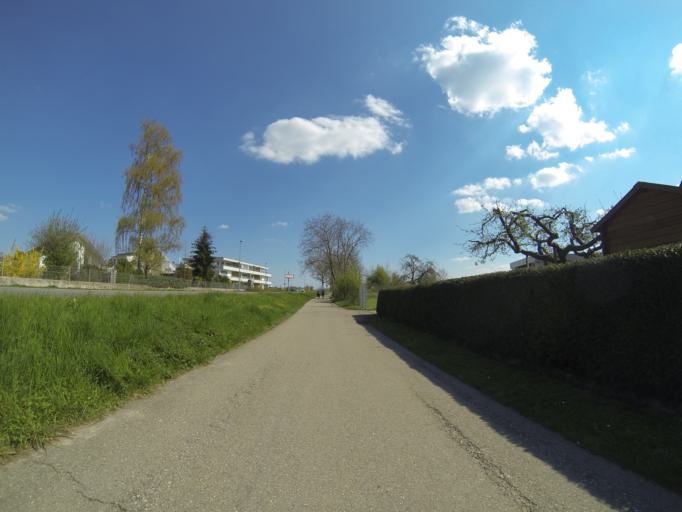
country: DE
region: Baden-Wuerttemberg
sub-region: Tuebingen Region
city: Laupheim
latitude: 48.2243
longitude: 9.8919
